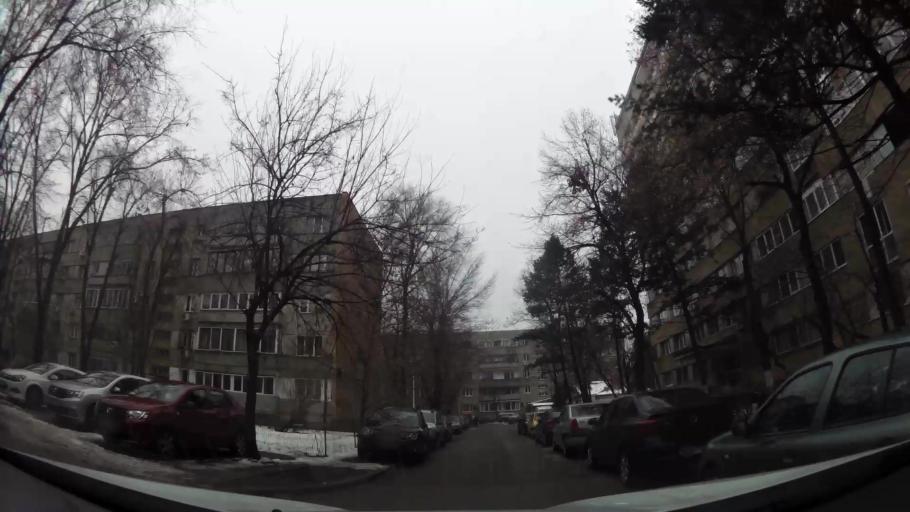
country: RO
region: Ilfov
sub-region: Comuna Chiajna
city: Rosu
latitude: 44.4360
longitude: 26.0159
